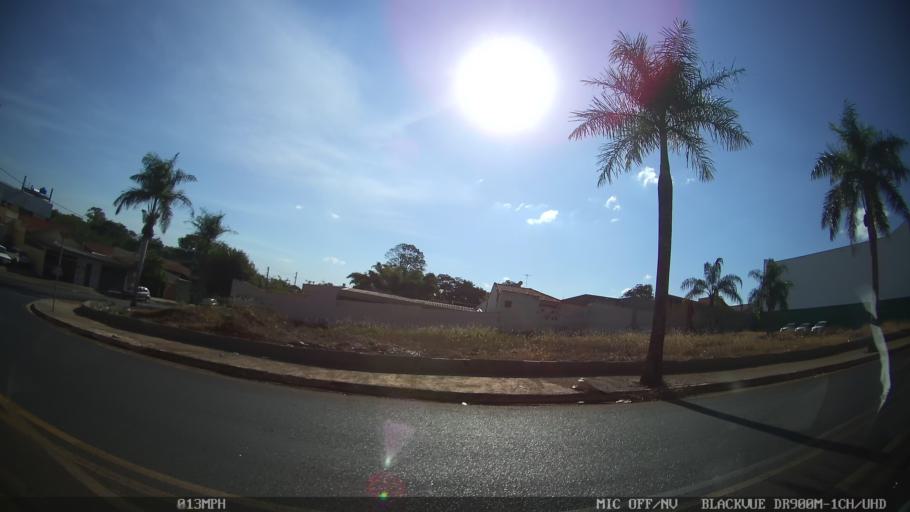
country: BR
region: Sao Paulo
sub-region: Ribeirao Preto
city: Ribeirao Preto
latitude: -21.1735
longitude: -47.7821
